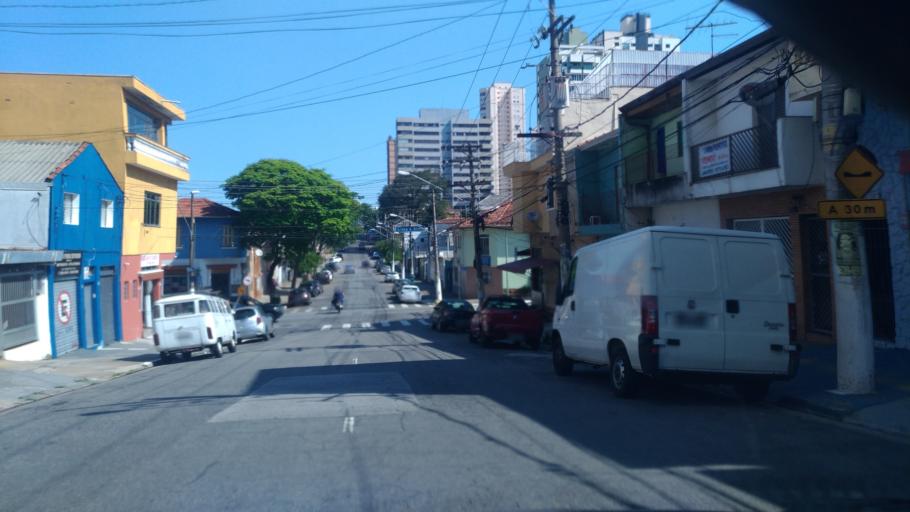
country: BR
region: Sao Paulo
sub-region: Sao Paulo
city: Sao Paulo
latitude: -23.5947
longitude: -46.6035
